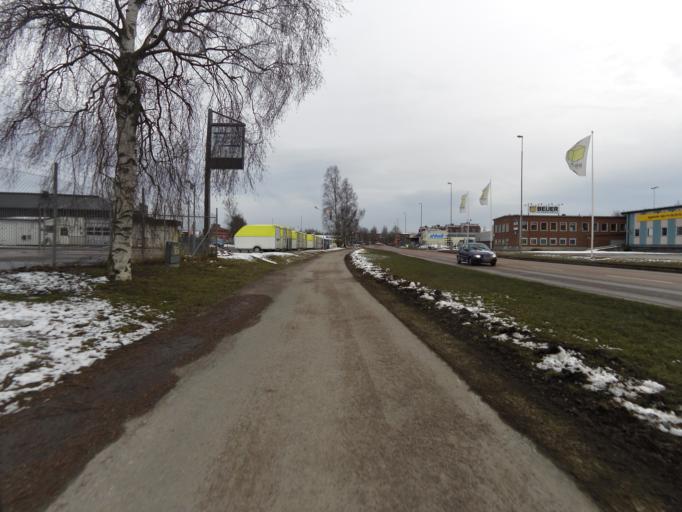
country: SE
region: Gaevleborg
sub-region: Gavle Kommun
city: Gavle
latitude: 60.6842
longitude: 17.1525
